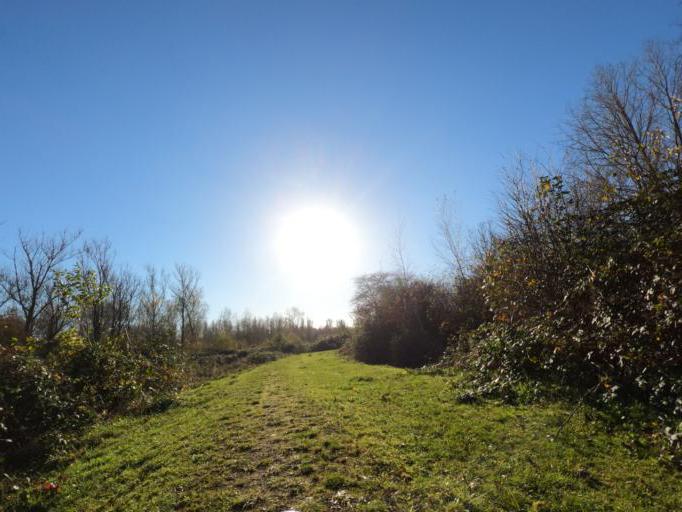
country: NL
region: Gelderland
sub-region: Gemeente Nijkerk
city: Nijkerk
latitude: 52.2685
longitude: 5.4429
